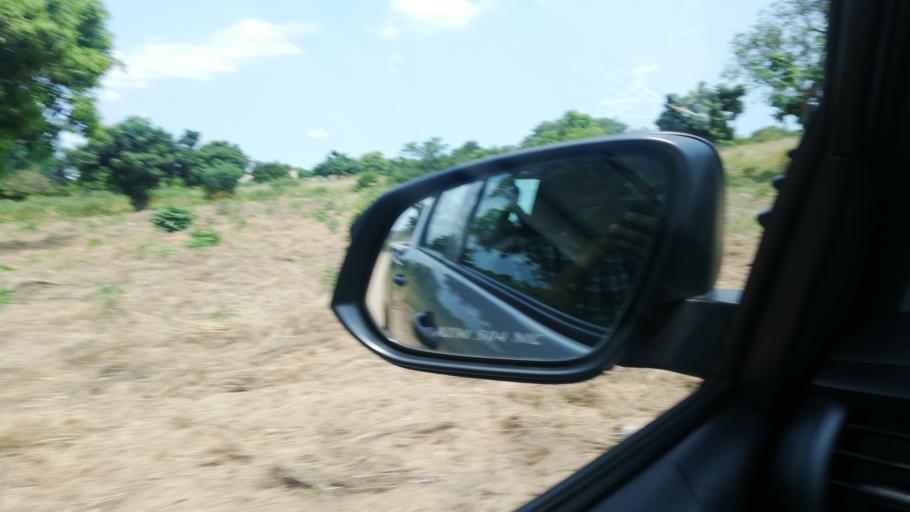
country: MZ
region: Maputo
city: Matola
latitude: -26.1105
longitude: 32.4280
